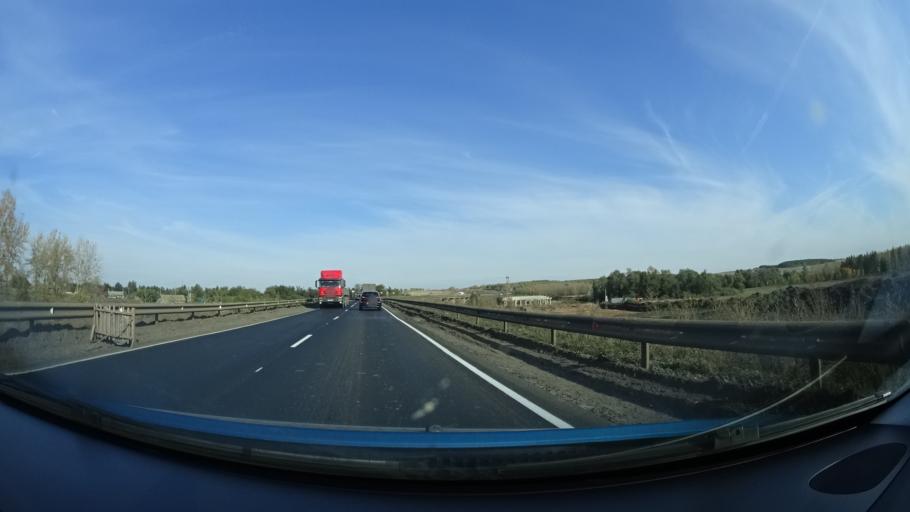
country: RU
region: Bashkortostan
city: Buzdyak
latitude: 54.6597
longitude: 54.6648
